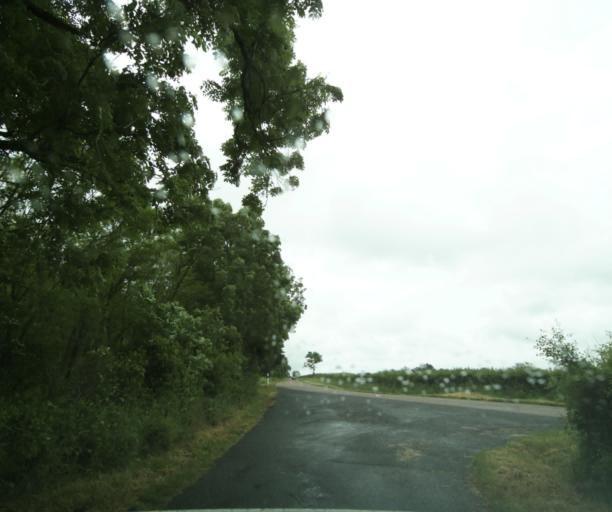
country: FR
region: Bourgogne
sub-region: Departement de Saone-et-Loire
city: Saint-Vallier
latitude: 46.4929
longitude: 4.4759
